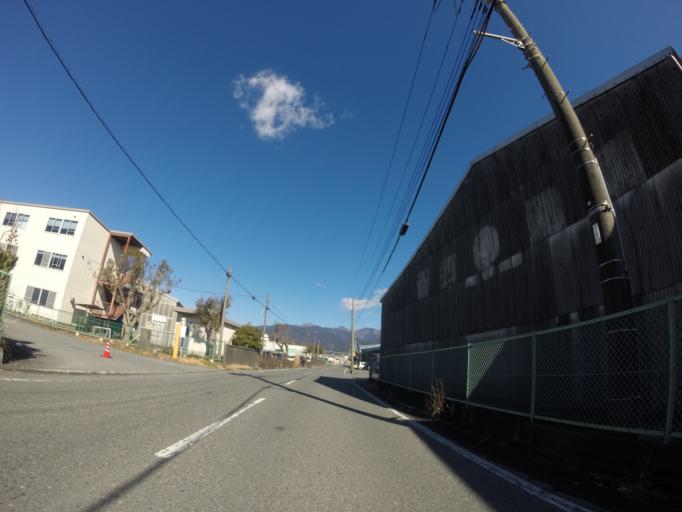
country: JP
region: Shizuoka
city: Fuji
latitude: 35.1525
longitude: 138.7166
